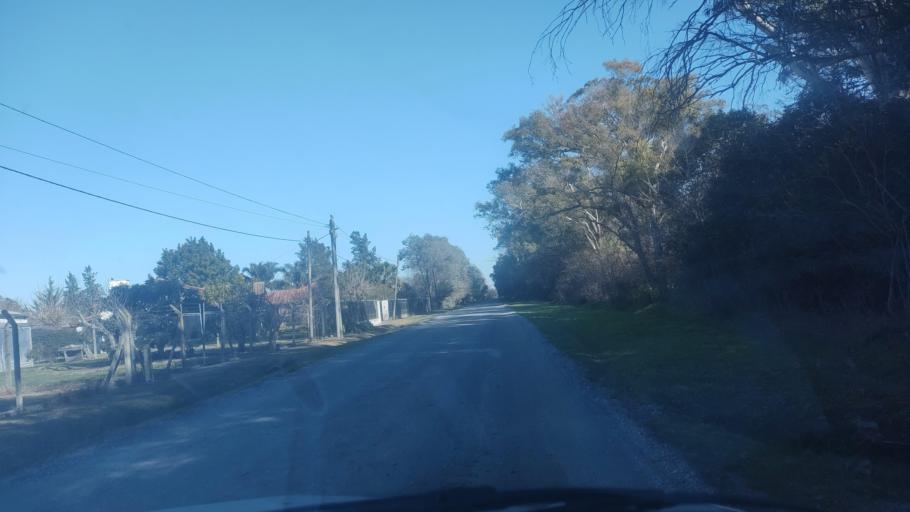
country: AR
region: Buenos Aires
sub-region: Partido de La Plata
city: La Plata
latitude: -34.8500
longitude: -58.1020
